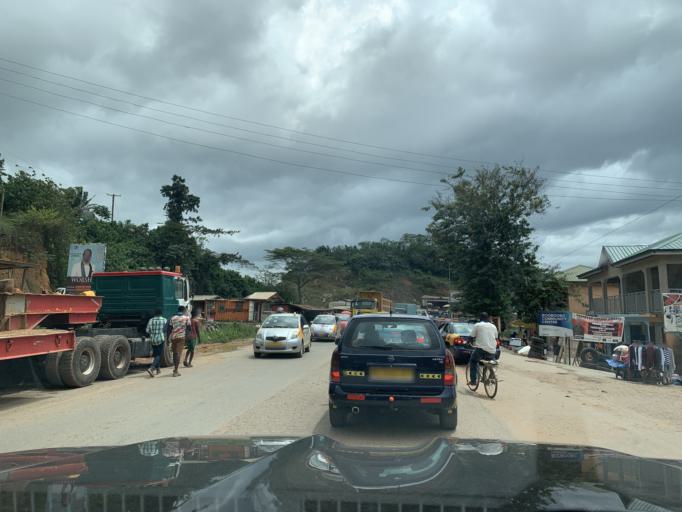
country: GH
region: Western
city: Tarkwa
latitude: 5.3277
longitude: -1.9812
